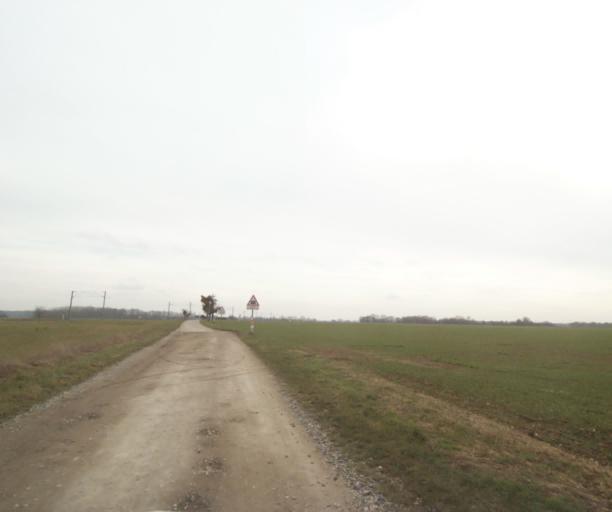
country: FR
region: Champagne-Ardenne
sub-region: Departement de la Haute-Marne
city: Villiers-en-Lieu
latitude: 48.6738
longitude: 4.8753
